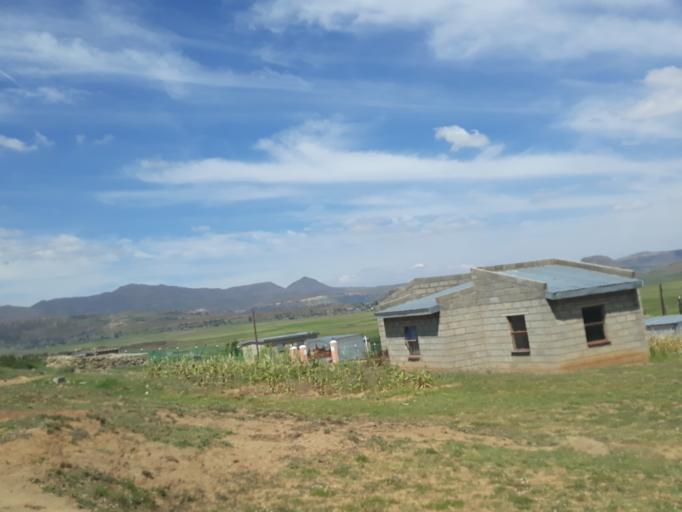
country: LS
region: Mohale's Hoek District
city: Mohale's Hoek
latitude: -30.1022
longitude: 27.4656
